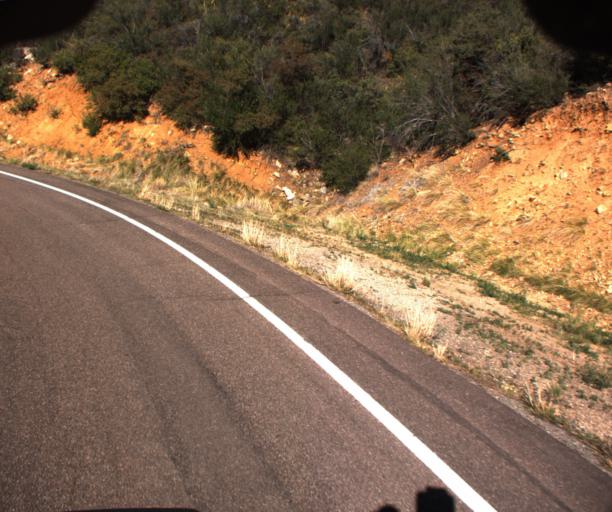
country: US
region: Arizona
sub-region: Yavapai County
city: Prescott
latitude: 34.4677
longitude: -112.5150
